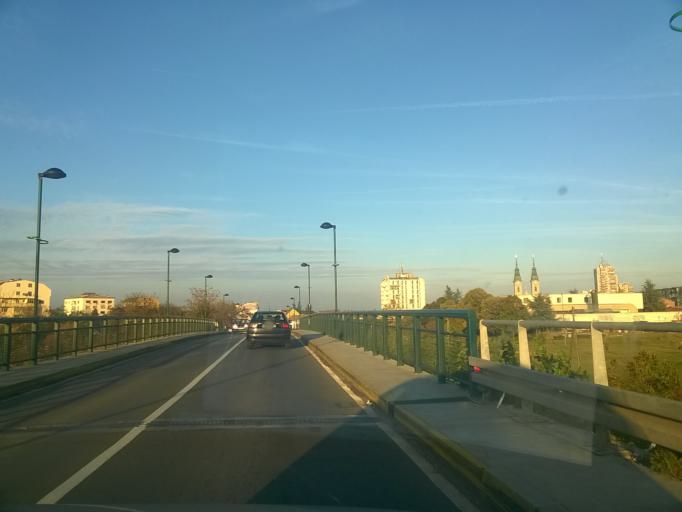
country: RS
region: Autonomna Pokrajina Vojvodina
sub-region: Juznobanatski Okrug
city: Pancevo
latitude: 44.8712
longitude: 20.6327
